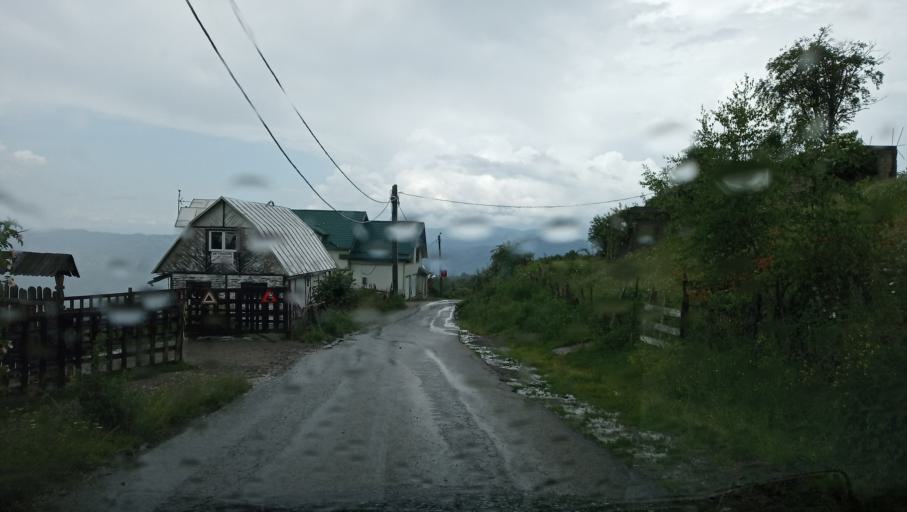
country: RO
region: Hunedoara
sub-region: Oras Petrila
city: Petrila
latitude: 45.3894
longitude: 23.4380
